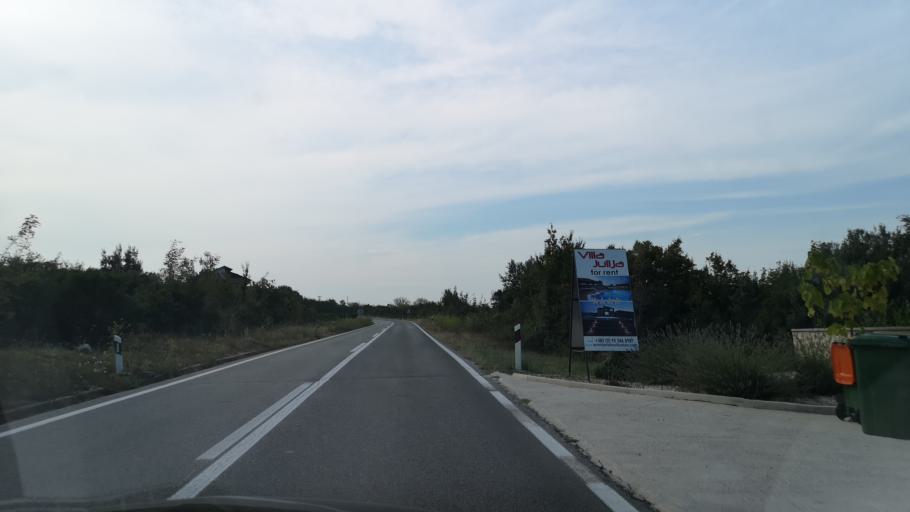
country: HR
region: Sibensko-Kniniska
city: Zaton
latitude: 43.8515
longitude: 15.7649
